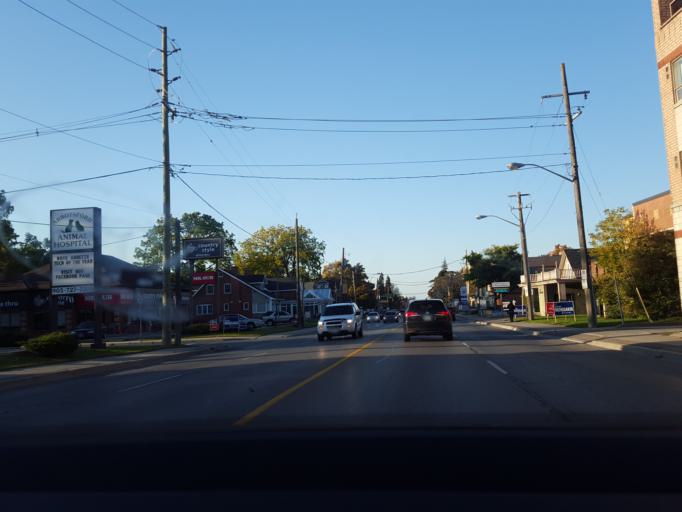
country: CA
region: Ontario
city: Newmarket
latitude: 43.9923
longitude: -79.4657
